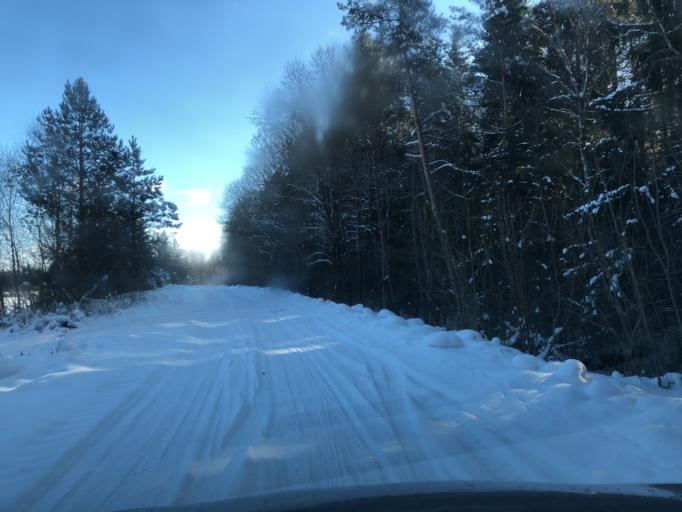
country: EE
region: Jaervamaa
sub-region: Paide linn
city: Paide
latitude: 59.0698
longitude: 25.5065
